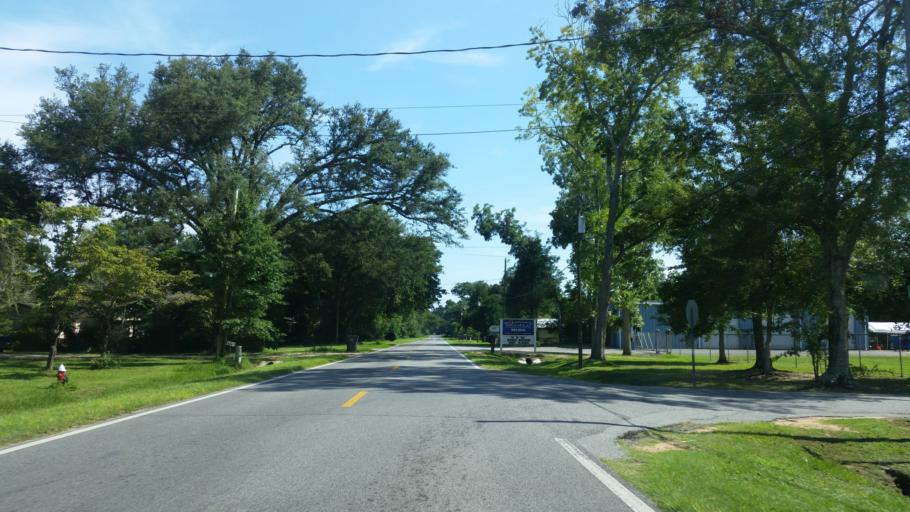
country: US
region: Florida
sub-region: Santa Rosa County
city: Pace
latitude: 30.5954
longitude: -87.1612
